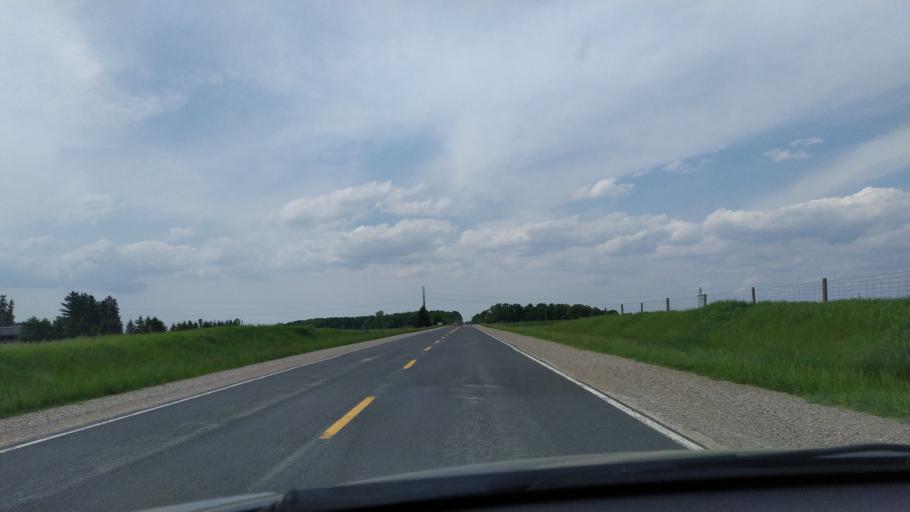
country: CA
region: Ontario
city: Ingersoll
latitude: 43.0351
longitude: -80.9754
